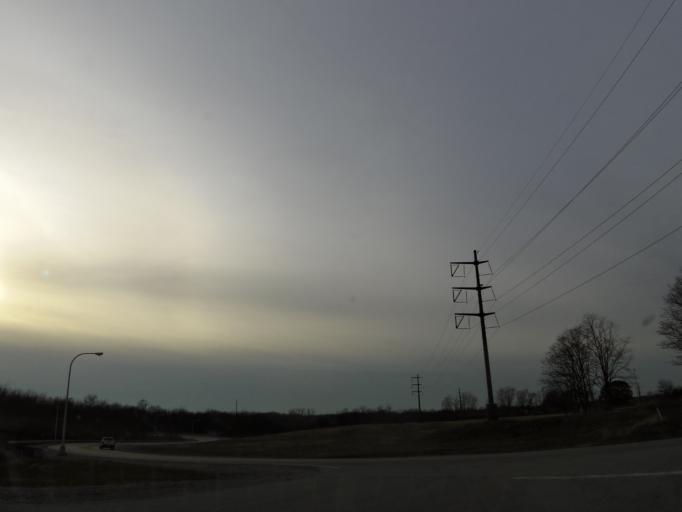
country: US
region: Kentucky
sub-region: Scott County
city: Georgetown
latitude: 38.2701
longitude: -84.5407
